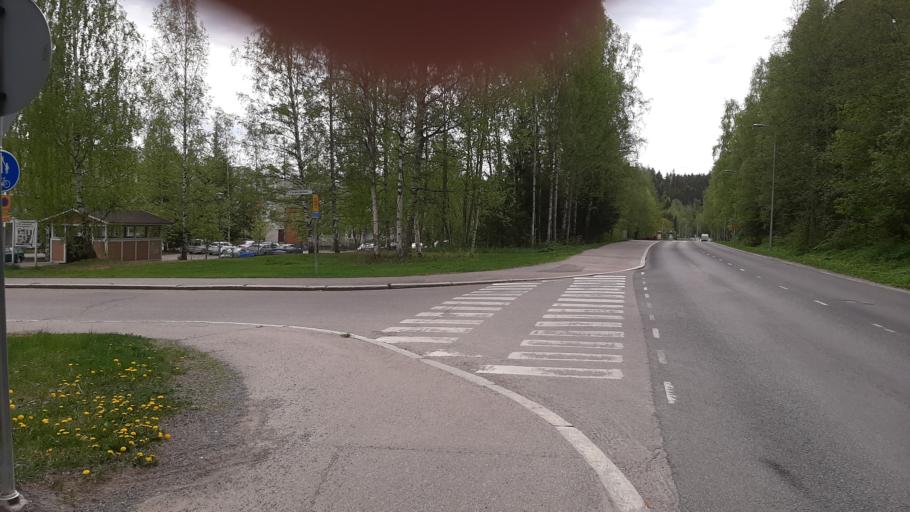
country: FI
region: Pirkanmaa
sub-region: Tampere
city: Tampere
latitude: 61.4668
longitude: 23.8539
